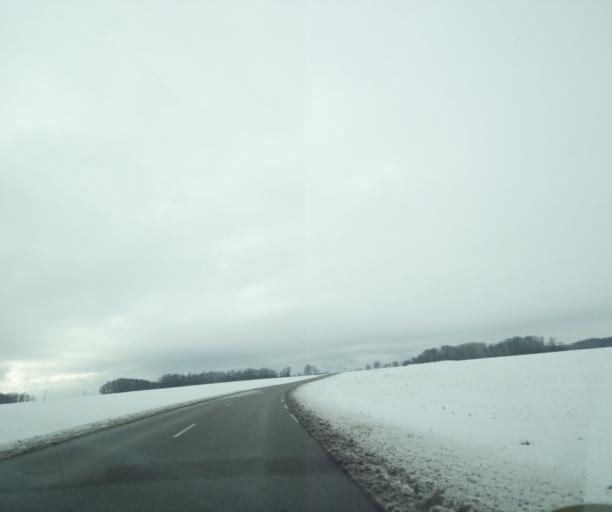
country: FR
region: Champagne-Ardenne
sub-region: Departement de la Haute-Marne
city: Montier-en-Der
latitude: 48.4566
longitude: 4.7479
